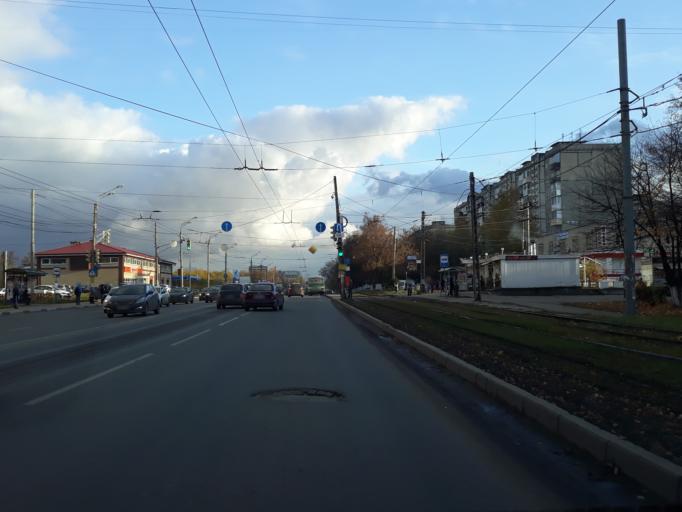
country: RU
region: Nizjnij Novgorod
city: Neklyudovo
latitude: 56.3418
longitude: 43.8776
